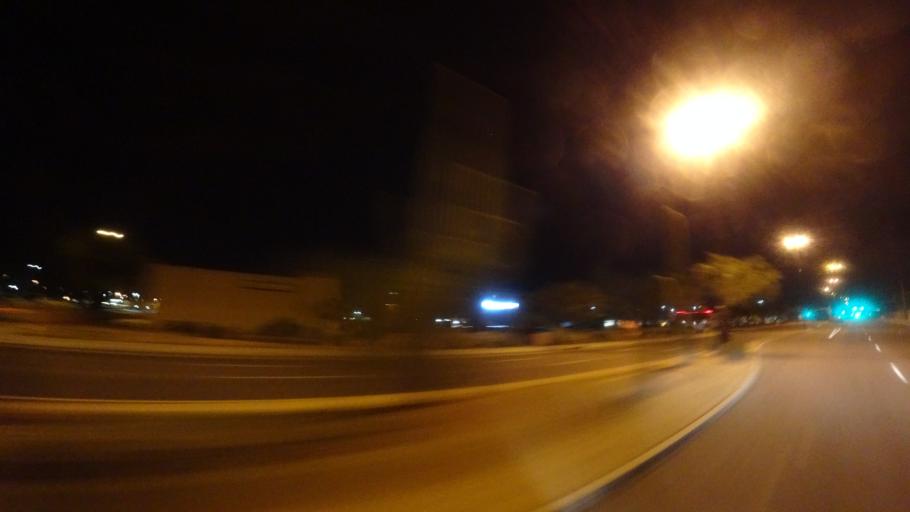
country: US
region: Arizona
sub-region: Maricopa County
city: Gilbert
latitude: 33.3940
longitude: -111.6860
